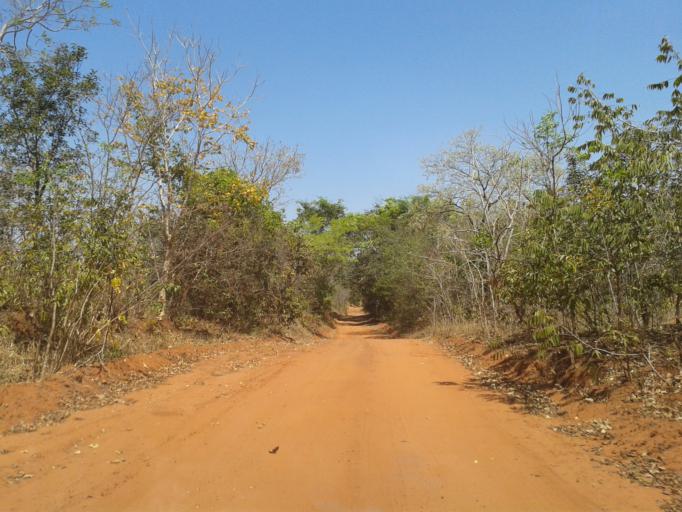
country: BR
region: Minas Gerais
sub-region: Ituiutaba
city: Ituiutaba
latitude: -19.0925
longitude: -49.2971
